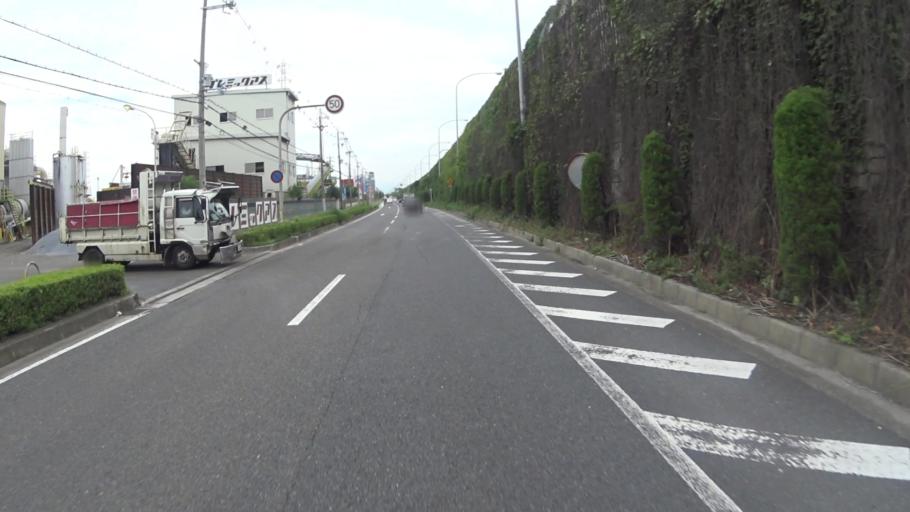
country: JP
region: Kyoto
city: Yawata
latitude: 34.9122
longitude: 135.7060
